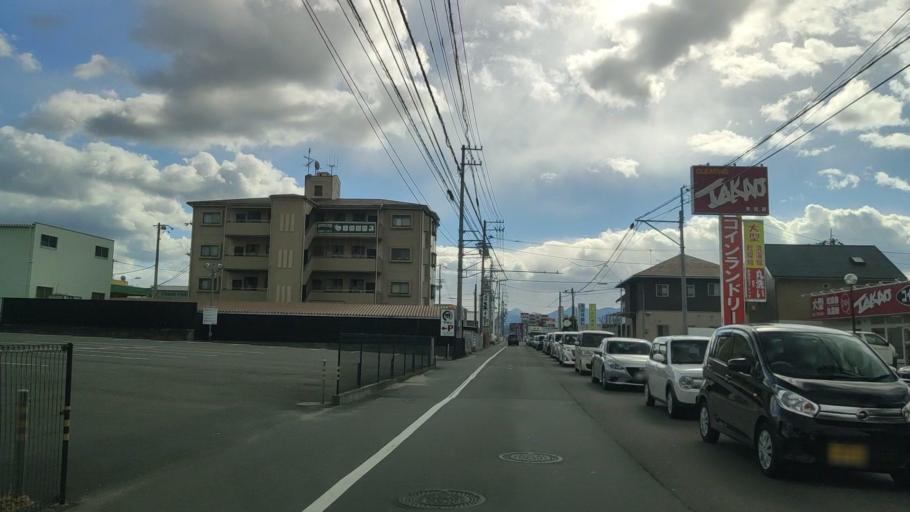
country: JP
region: Ehime
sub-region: Shikoku-chuo Shi
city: Matsuyama
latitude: 33.8136
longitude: 132.7953
